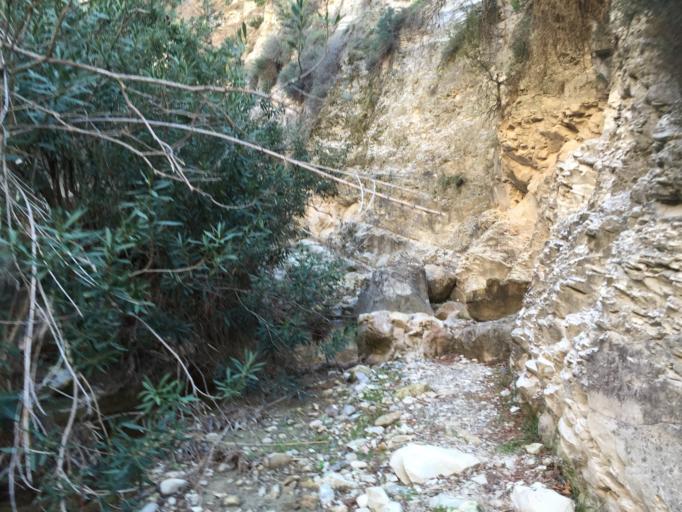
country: CY
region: Pafos
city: Pegeia
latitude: 34.9262
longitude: 32.3599
